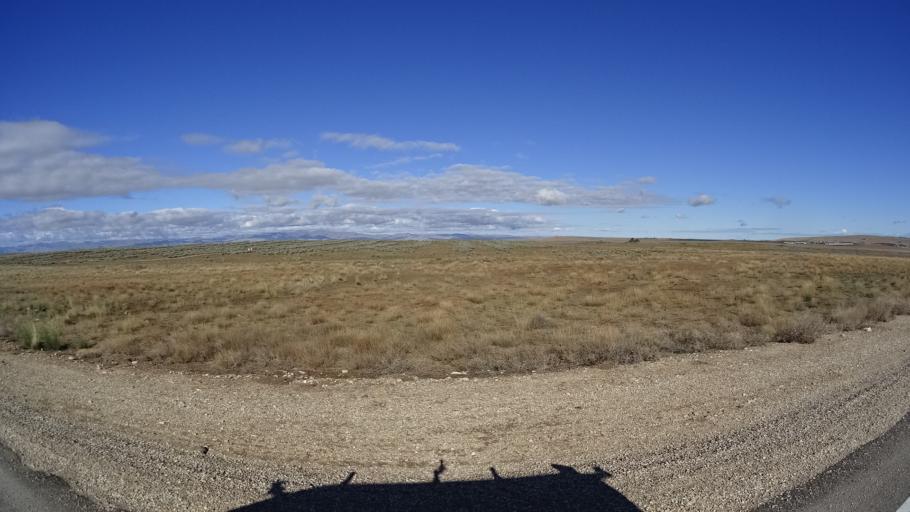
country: US
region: Idaho
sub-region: Ada County
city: Kuna
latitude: 43.3945
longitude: -116.4139
